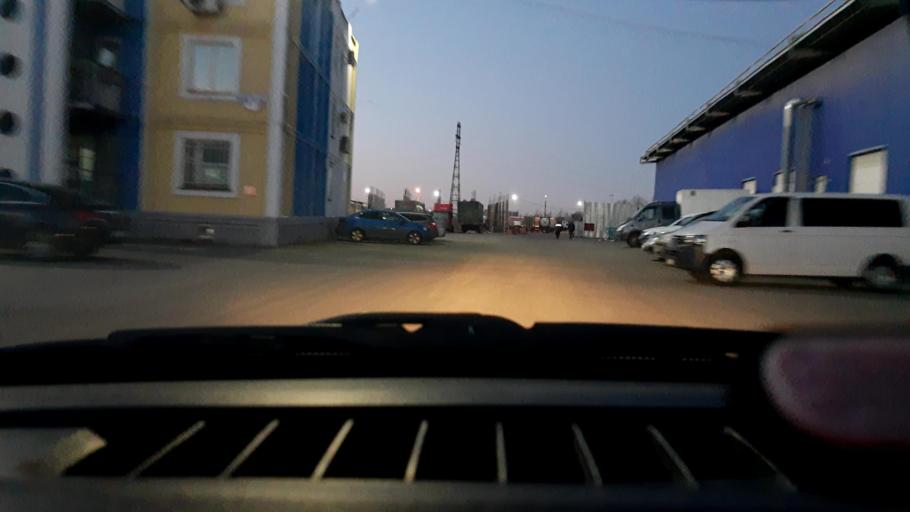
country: RU
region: Nizjnij Novgorod
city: Nizhniy Novgorod
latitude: 56.2478
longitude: 43.9344
